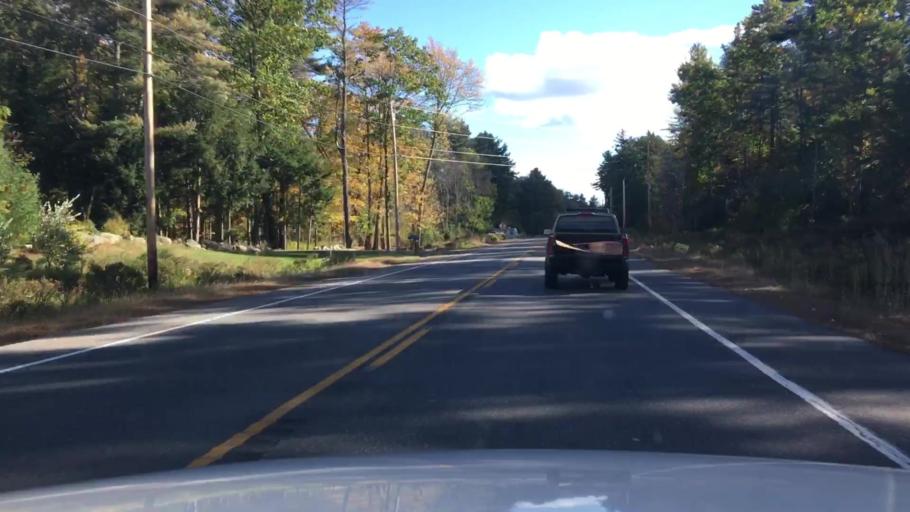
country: US
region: Maine
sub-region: York County
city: Wells Beach Station
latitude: 43.3508
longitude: -70.6476
